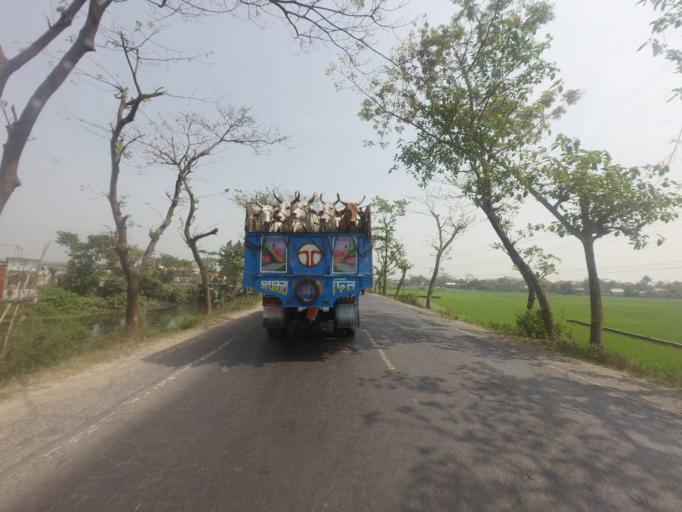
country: BD
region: Dhaka
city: Bhairab Bazar
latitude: 24.0483
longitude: 91.0964
